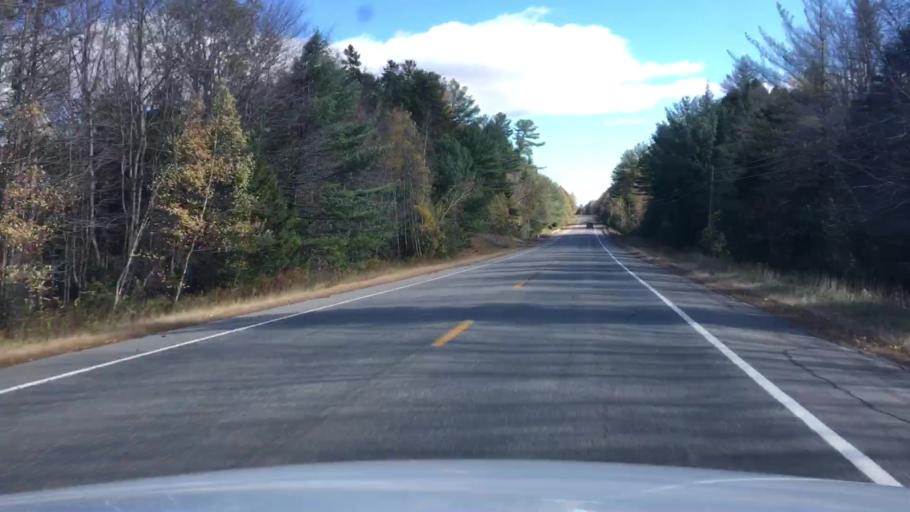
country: US
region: Maine
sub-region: Penobscot County
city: Millinocket
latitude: 45.6569
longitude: -68.6687
